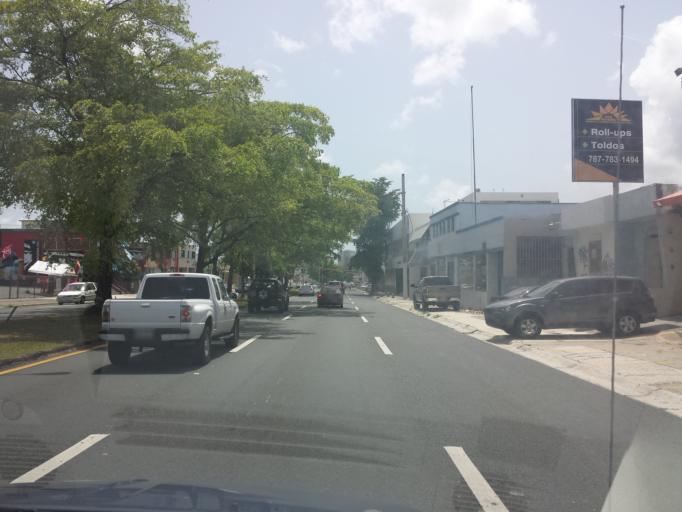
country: PR
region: Catano
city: Catano
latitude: 18.4053
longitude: -66.0807
